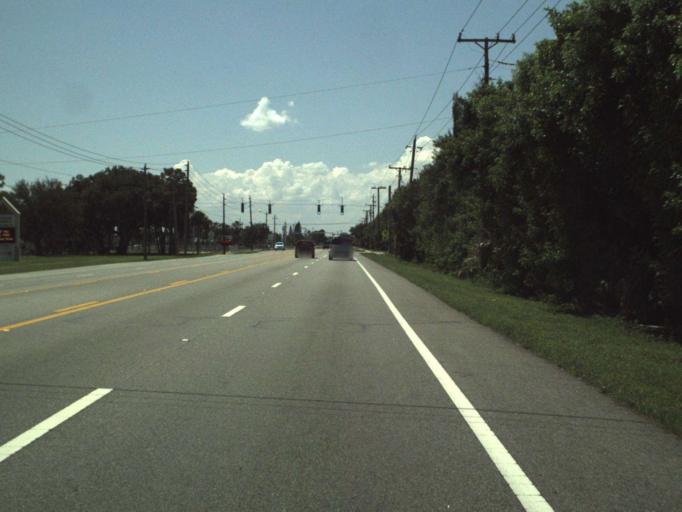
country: US
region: Florida
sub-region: Brevard County
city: Cocoa
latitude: 28.3926
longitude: -80.7040
